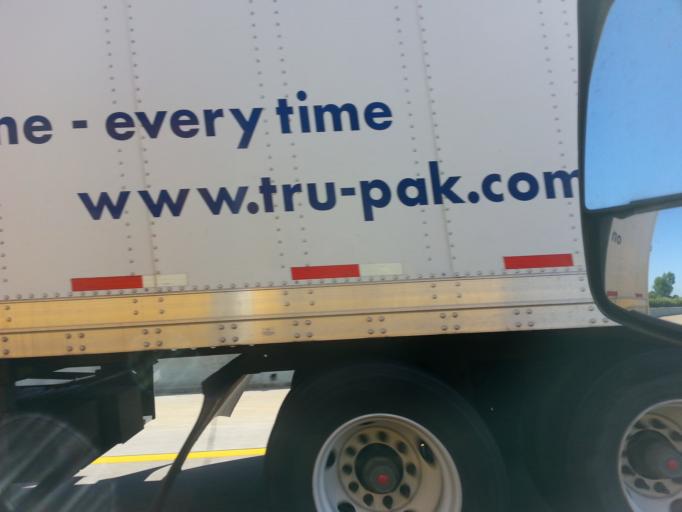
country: US
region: Kentucky
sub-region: Jefferson County
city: Saint Regis Park
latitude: 38.2359
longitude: -85.6171
